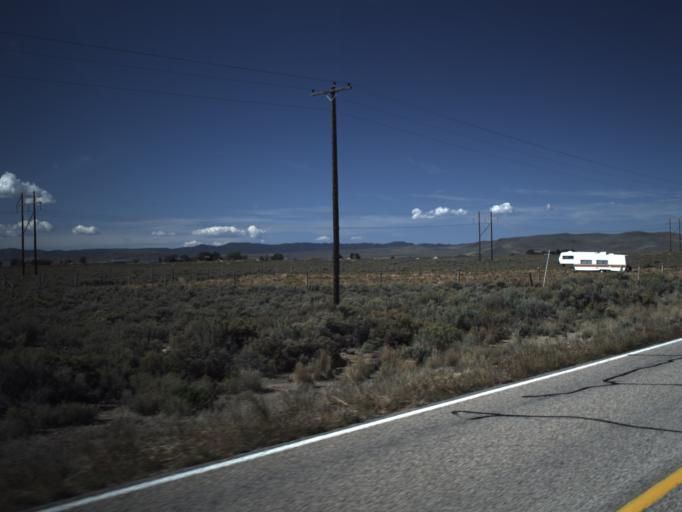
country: US
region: Utah
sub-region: Washington County
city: Enterprise
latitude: 37.7036
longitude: -113.6398
